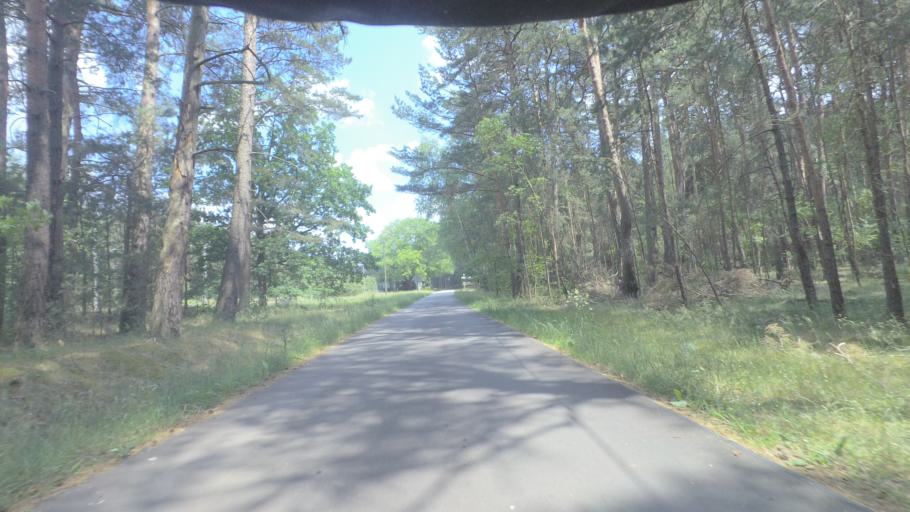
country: DE
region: Brandenburg
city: Borkheide
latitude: 52.2366
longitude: 12.8688
